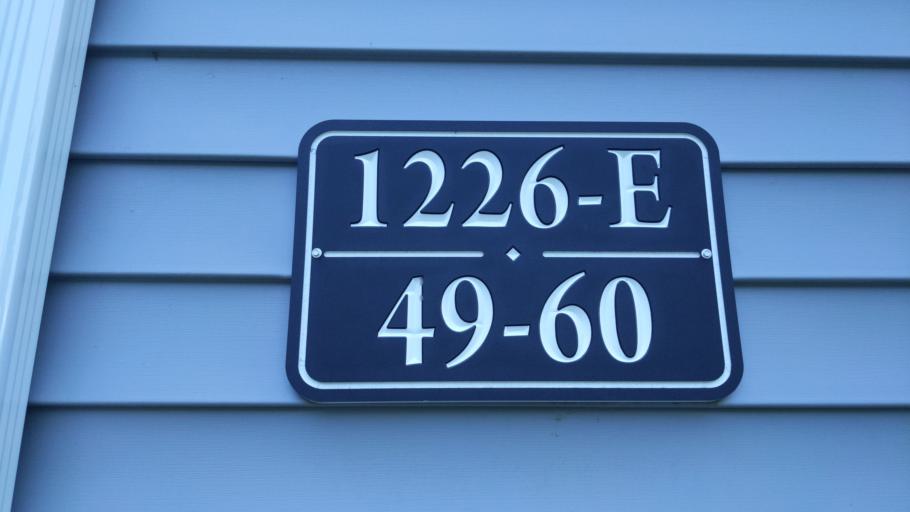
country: US
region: Virginia
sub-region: Montgomery County
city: Blacksburg
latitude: 37.2414
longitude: -80.4333
